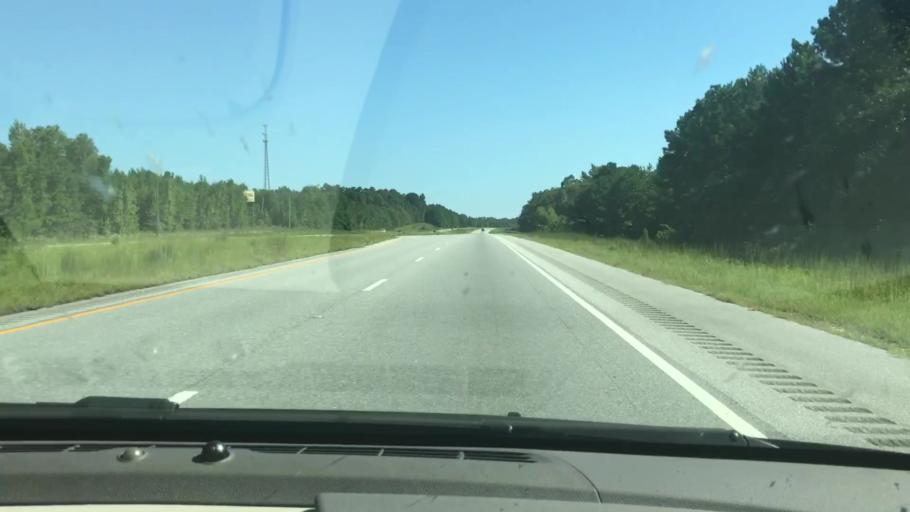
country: US
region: Alabama
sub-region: Russell County
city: Ladonia
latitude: 32.3841
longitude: -85.0810
